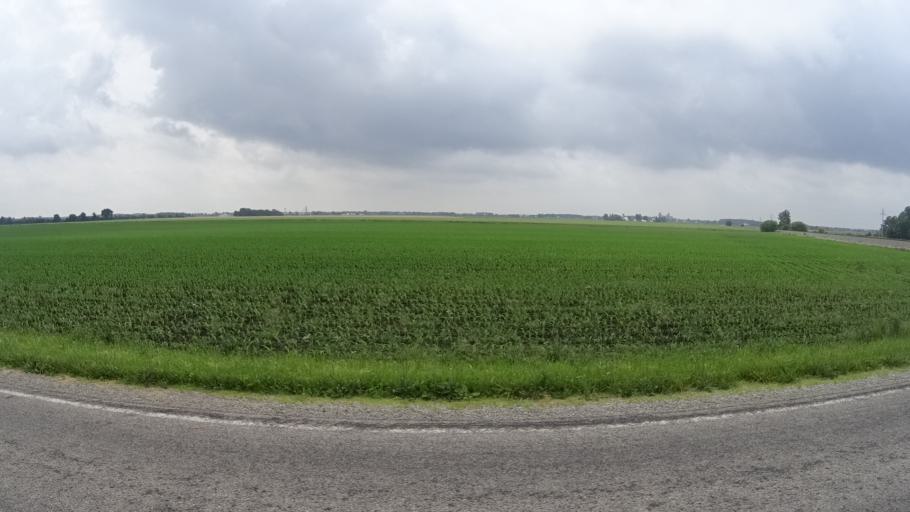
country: US
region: Ohio
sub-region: Huron County
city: Bellevue
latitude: 41.3255
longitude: -82.7983
